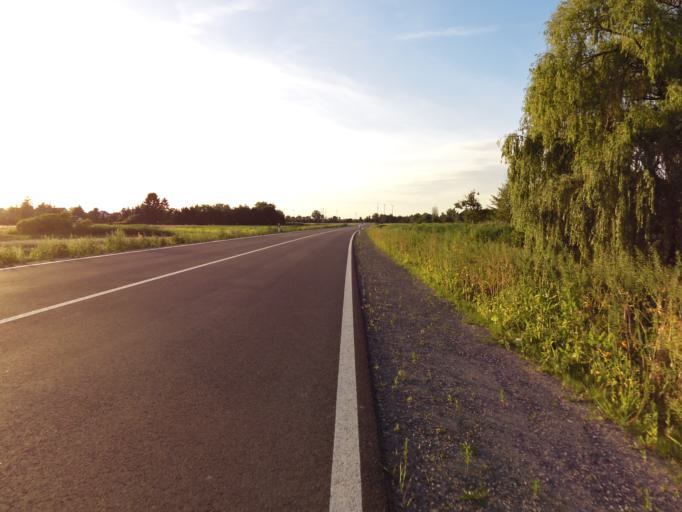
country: DE
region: Rheinland-Pfalz
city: Hessheim
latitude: 49.5465
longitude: 8.3133
